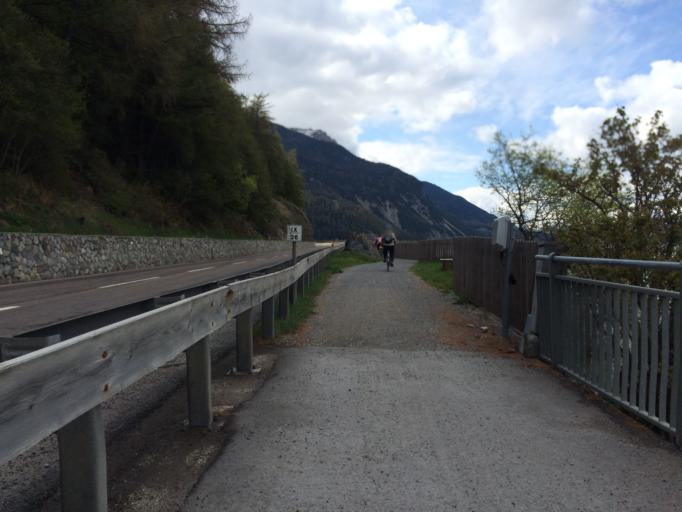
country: IT
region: Trentino-Alto Adige
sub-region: Bolzano
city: Curon Venosta
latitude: 46.8166
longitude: 10.5320
